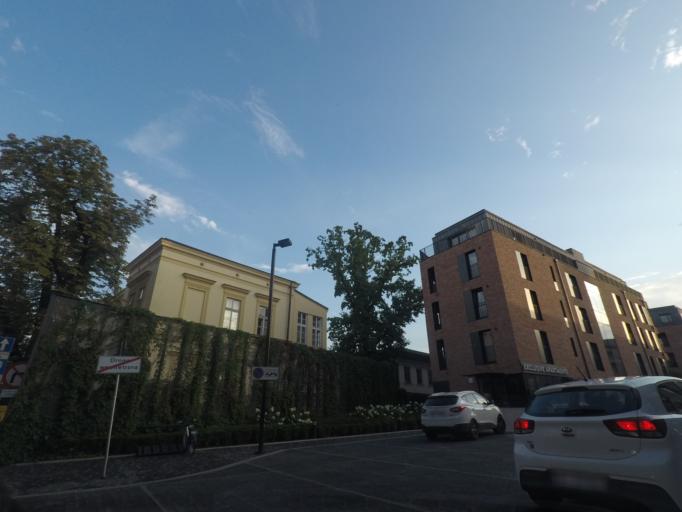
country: PL
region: Lesser Poland Voivodeship
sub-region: Krakow
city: Krakow
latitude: 50.0640
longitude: 19.9503
